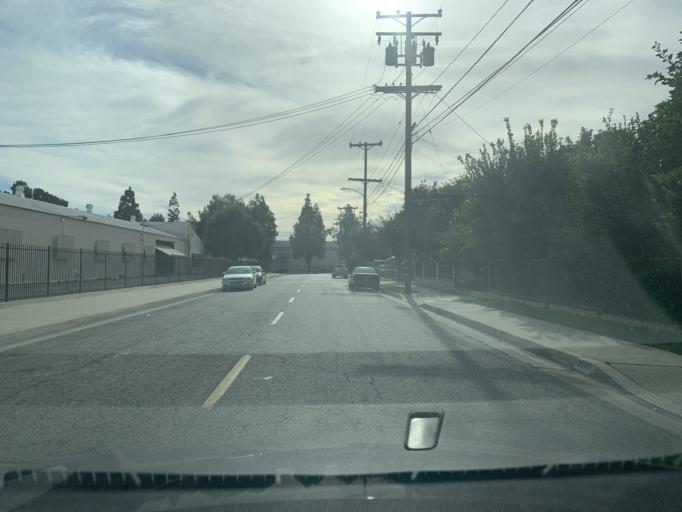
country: US
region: California
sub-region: Los Angeles County
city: South El Monte
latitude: 34.0742
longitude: -118.0510
